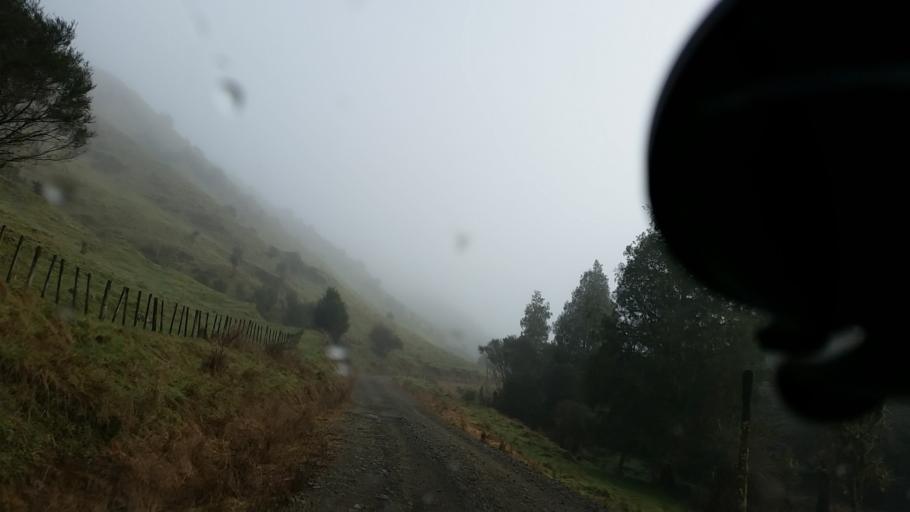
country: NZ
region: Taranaki
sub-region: New Plymouth District
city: Waitara
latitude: -38.9705
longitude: 174.7987
